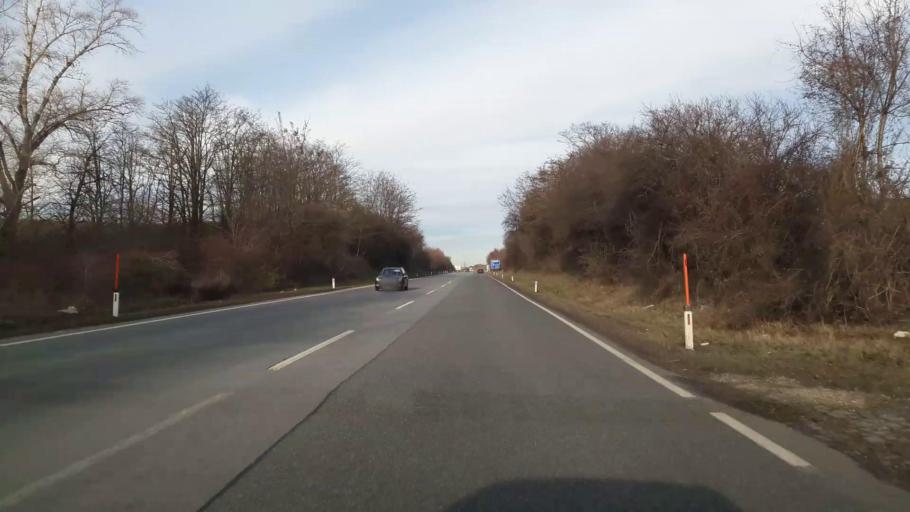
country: AT
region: Lower Austria
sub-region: Politischer Bezirk Mistelbach
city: Gaweinstal
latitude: 48.4889
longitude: 16.5957
